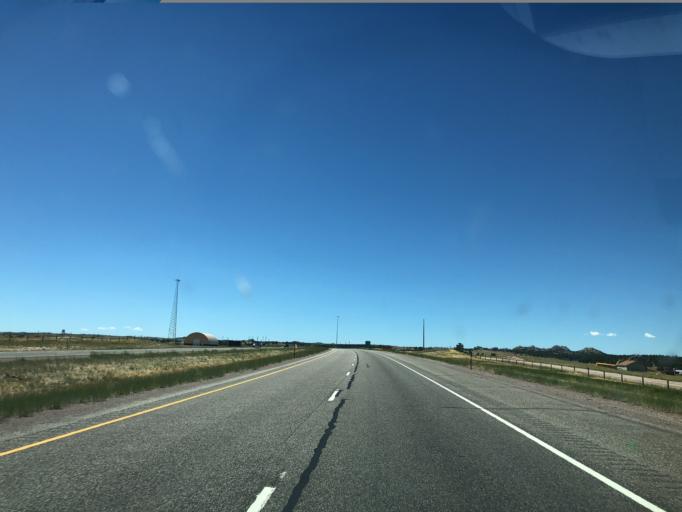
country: US
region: Wyoming
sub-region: Albany County
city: Laramie
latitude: 41.1234
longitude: -105.2936
